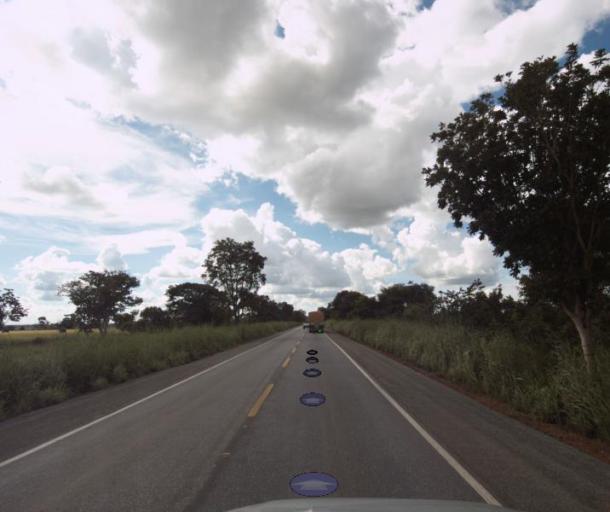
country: BR
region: Goias
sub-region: Porangatu
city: Porangatu
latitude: -13.2814
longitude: -49.1279
